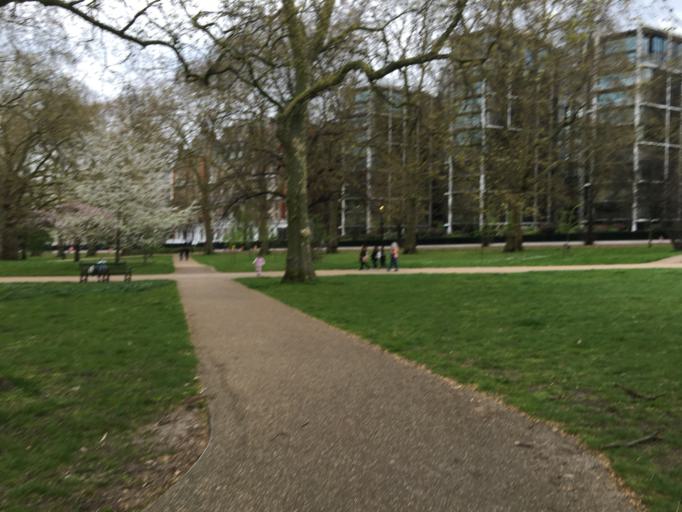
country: GB
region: England
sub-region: Greater London
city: Chelsea
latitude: 51.5033
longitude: -0.1622
